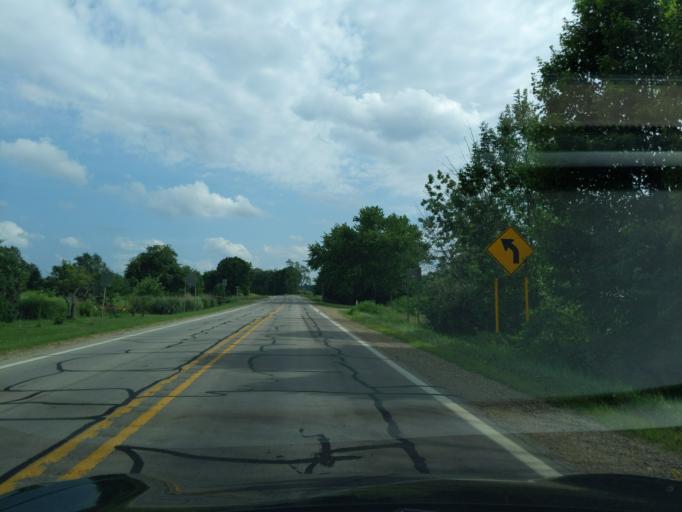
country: US
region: Michigan
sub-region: Eaton County
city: Eaton Rapids
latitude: 42.4090
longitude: -84.6041
